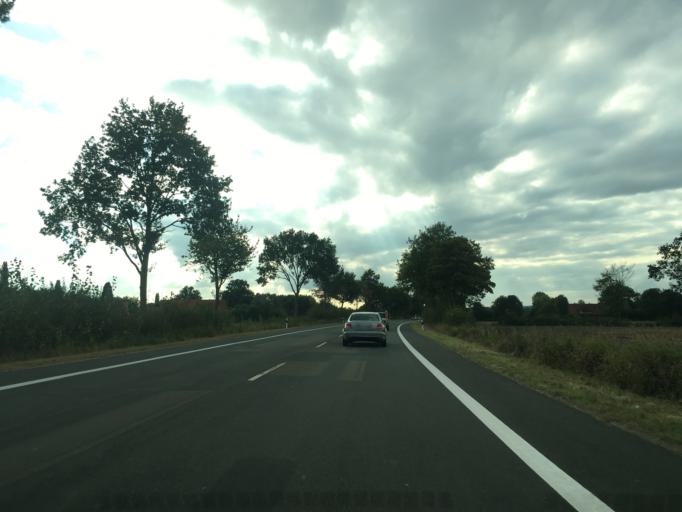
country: DE
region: North Rhine-Westphalia
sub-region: Regierungsbezirk Munster
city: Muenster
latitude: 51.9856
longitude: 7.5365
